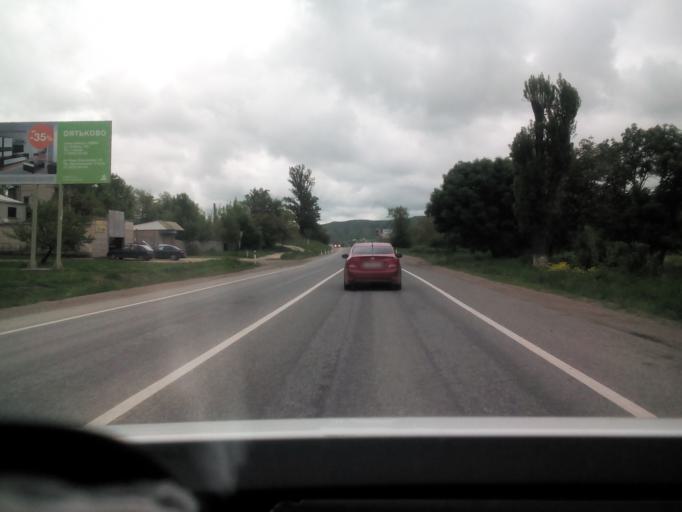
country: RU
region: Stavropol'skiy
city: Yasnaya Polyana
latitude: 43.9600
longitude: 42.7670
